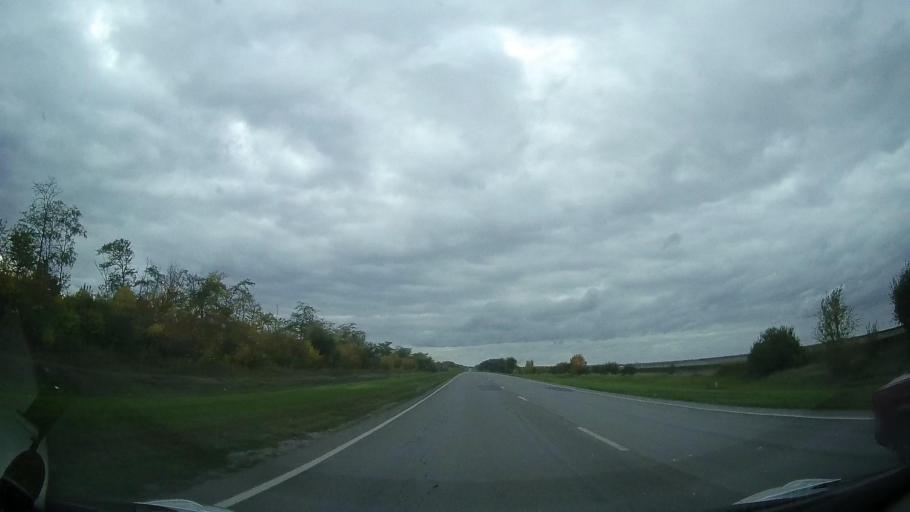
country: RU
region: Rostov
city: Yegorlykskaya
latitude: 46.5480
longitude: 40.7447
